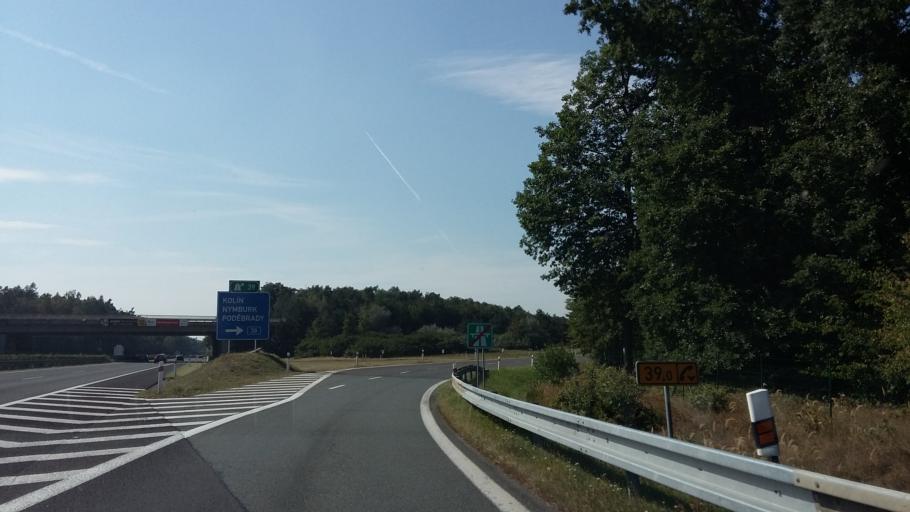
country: CZ
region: Central Bohemia
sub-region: Okres Nymburk
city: Podebrady
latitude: 50.1180
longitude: 15.1274
